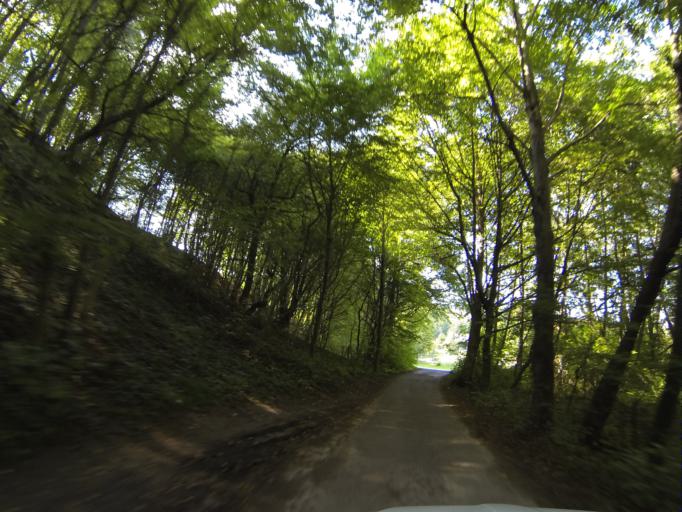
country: SK
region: Nitriansky
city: Bojnice
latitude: 48.7970
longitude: 18.5791
